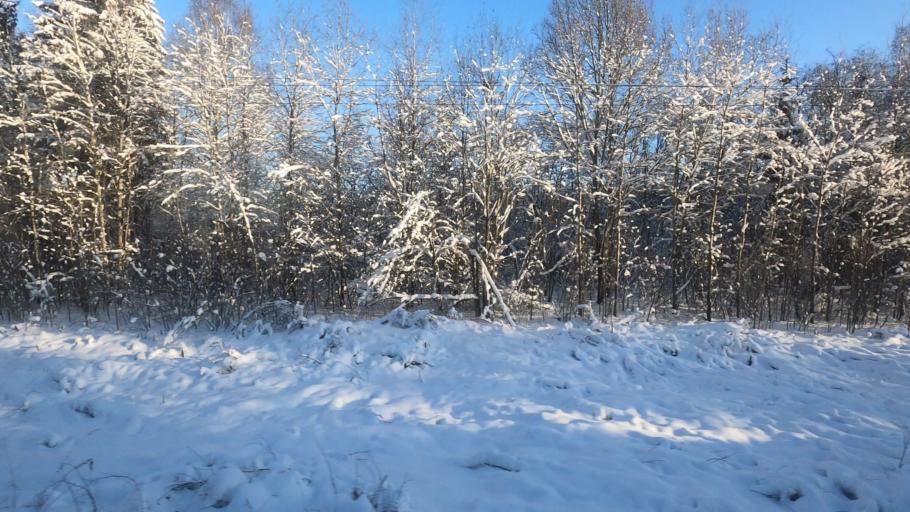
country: RU
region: Moskovskaya
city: Novo-Nikol'skoye
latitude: 56.6352
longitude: 37.5624
